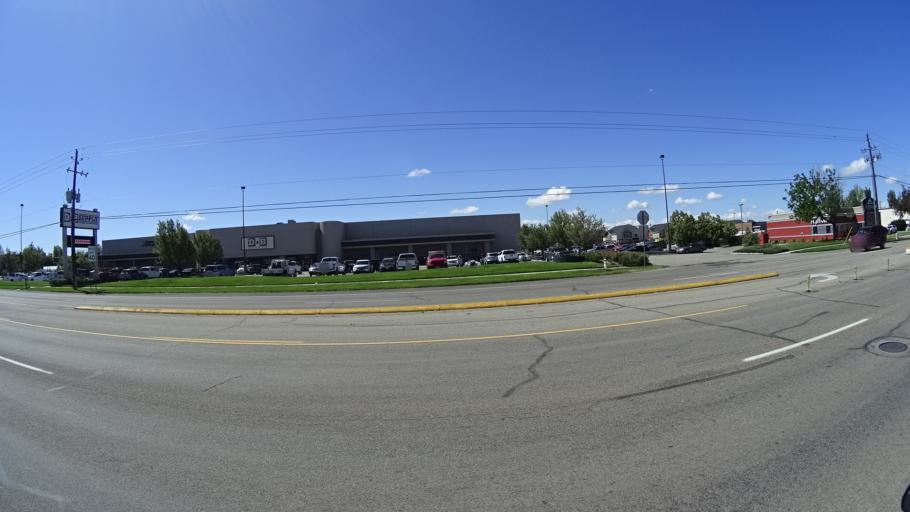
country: US
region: Idaho
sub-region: Ada County
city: Meridian
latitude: 43.6193
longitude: -116.3724
